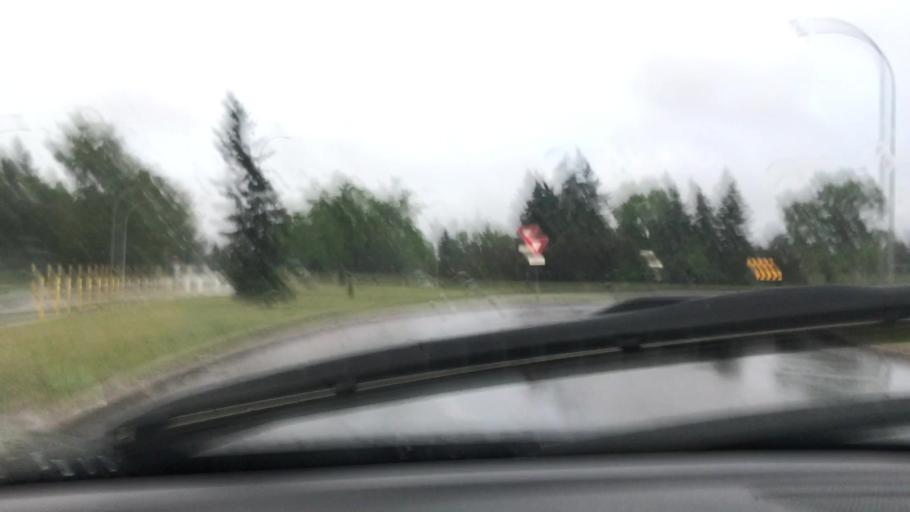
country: CA
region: Alberta
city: Sherwood Park
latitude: 53.5195
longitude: -113.3182
